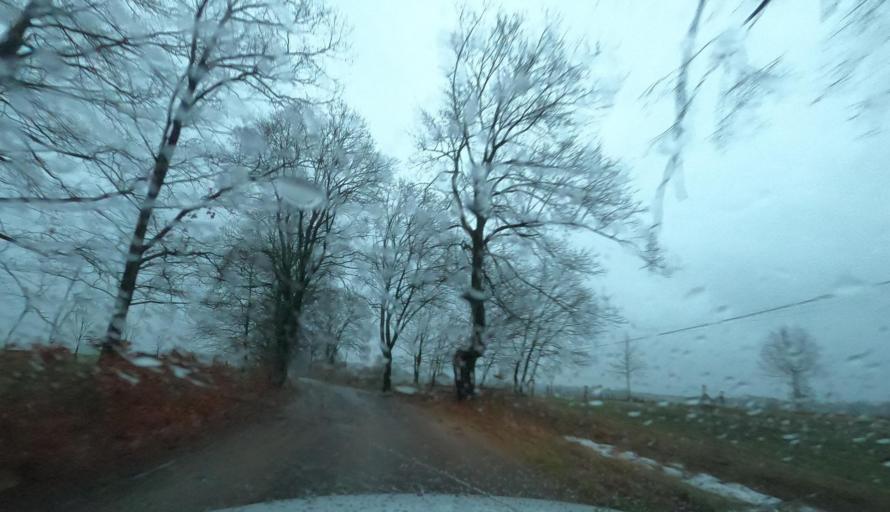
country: PL
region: West Pomeranian Voivodeship
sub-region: Powiat szczecinecki
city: Borne Sulinowo
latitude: 53.6858
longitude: 16.4813
